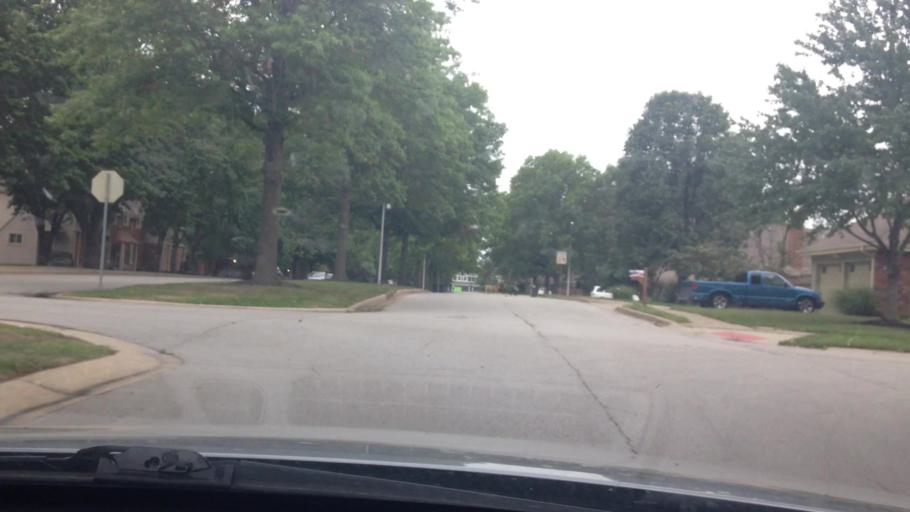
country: US
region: Missouri
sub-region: Platte County
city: Weatherby Lake
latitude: 39.2463
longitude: -94.6430
